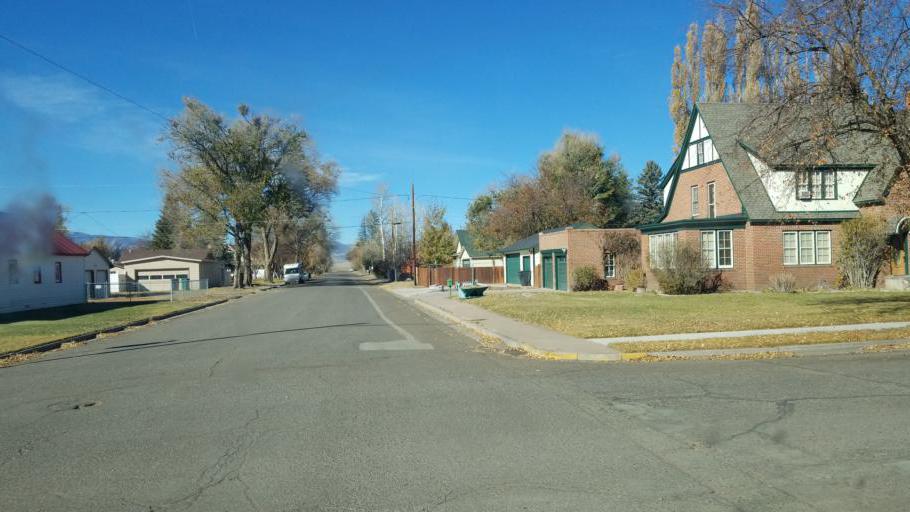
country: US
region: Colorado
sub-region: Rio Grande County
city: Monte Vista
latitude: 37.5779
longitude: -106.1537
